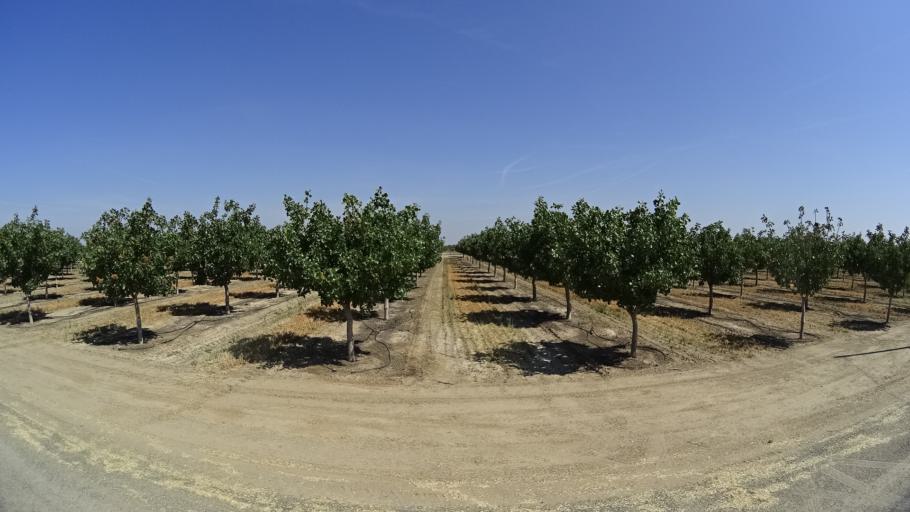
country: US
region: California
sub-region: Kings County
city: Lemoore
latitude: 36.3280
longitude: -119.8185
